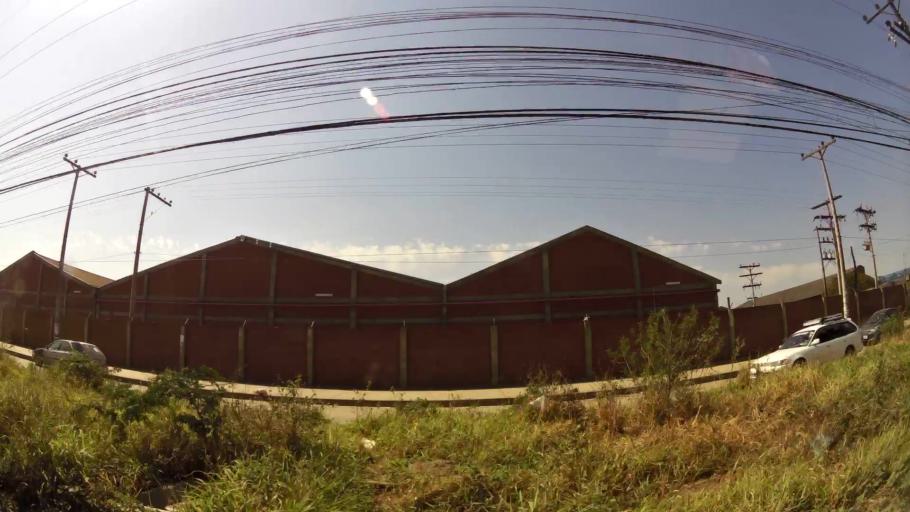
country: BO
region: Santa Cruz
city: Santa Cruz de la Sierra
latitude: -17.7589
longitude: -63.1412
